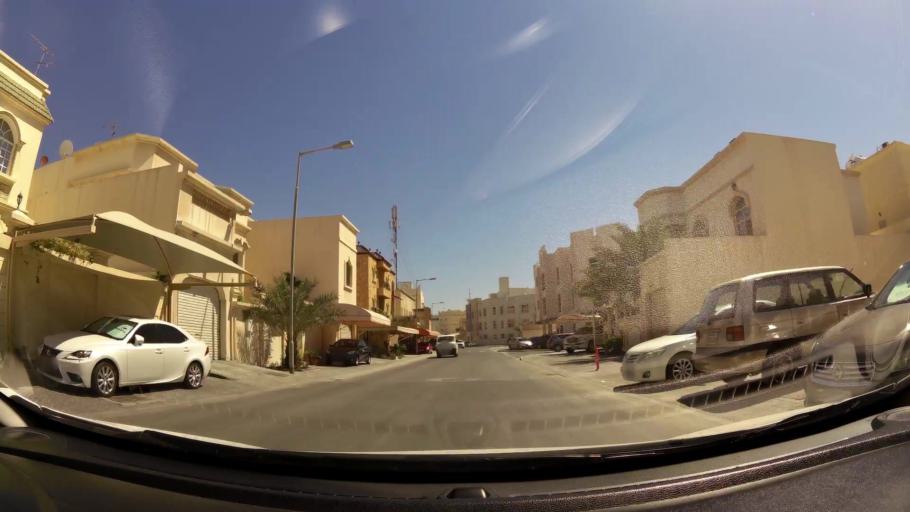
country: BH
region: Muharraq
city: Al Muharraq
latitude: 26.2766
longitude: 50.6072
